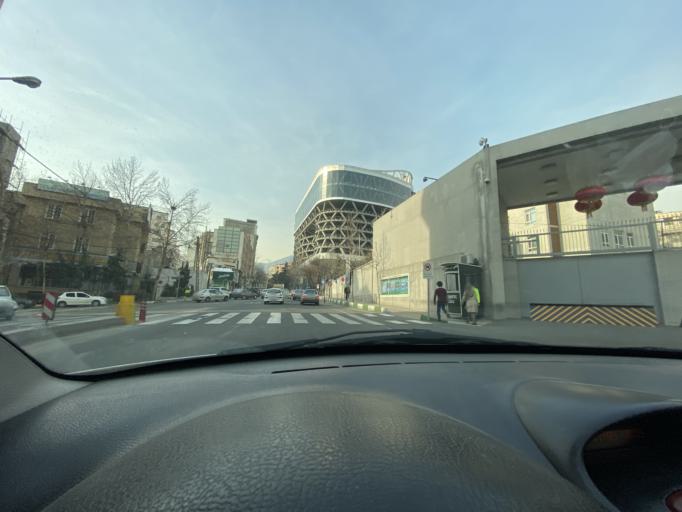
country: IR
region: Tehran
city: Tajrish
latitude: 35.8040
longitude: 51.4776
